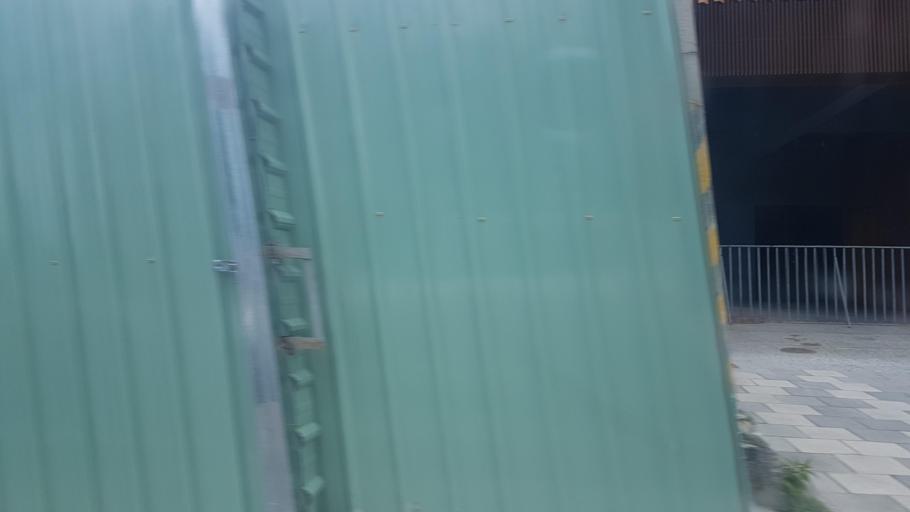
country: TW
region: Taiwan
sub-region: Hualien
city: Hualian
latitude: 23.9945
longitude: 121.6335
